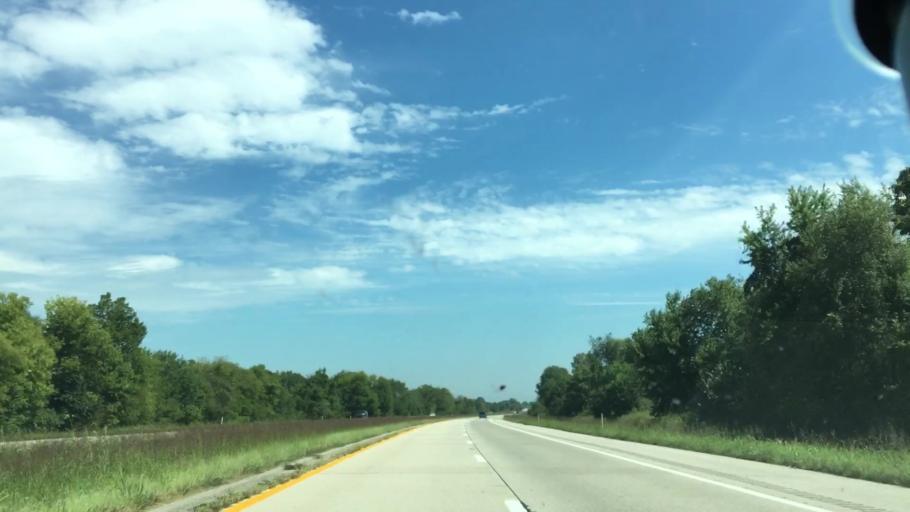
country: US
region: Kentucky
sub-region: Daviess County
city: Owensboro
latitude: 37.7684
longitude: -87.1985
